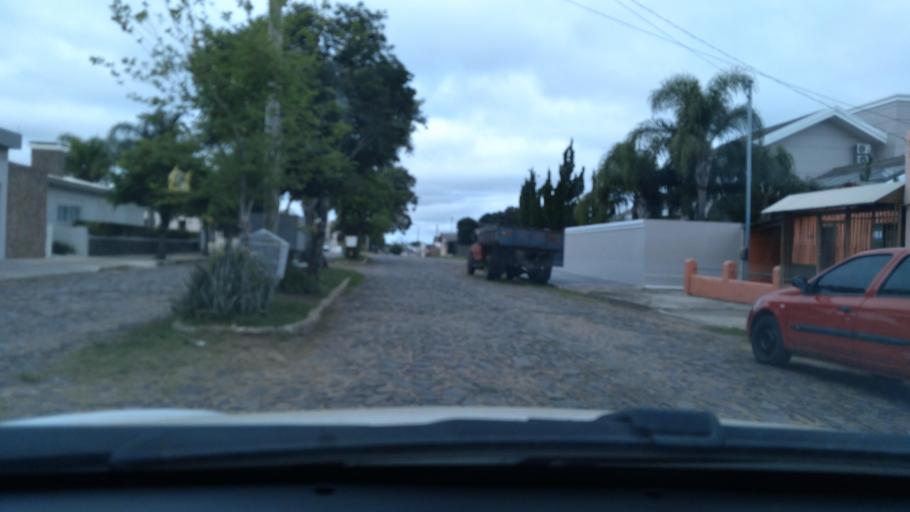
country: BR
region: Rio Grande do Sul
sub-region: Dom Pedrito
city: Dom Pedrito
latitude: -30.9812
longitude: -54.6684
